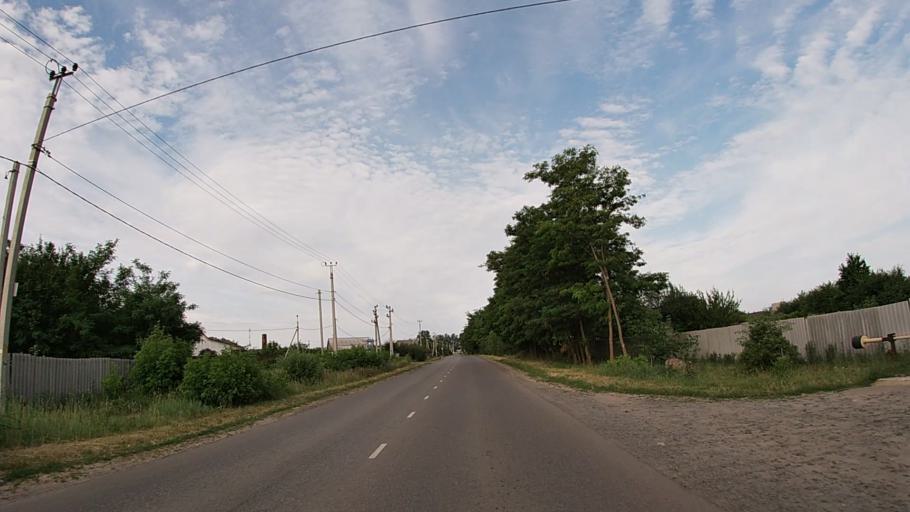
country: RU
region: Belgorod
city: Severnyy
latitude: 50.6916
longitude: 36.5632
